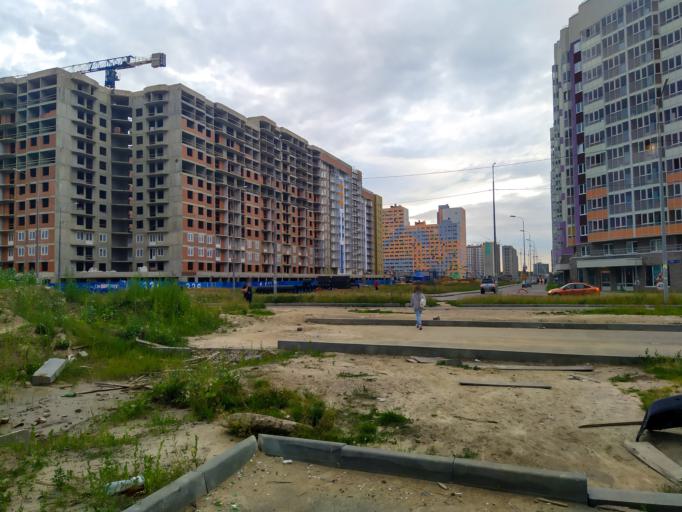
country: RU
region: Leningrad
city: Murino
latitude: 60.0564
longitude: 30.4355
